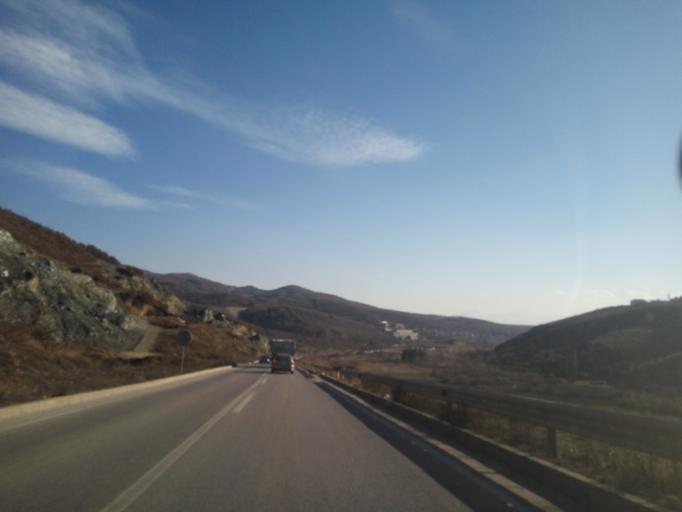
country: XK
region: Pristina
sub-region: Komuna e Prishtines
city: Pristina
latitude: 42.6174
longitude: 21.2210
